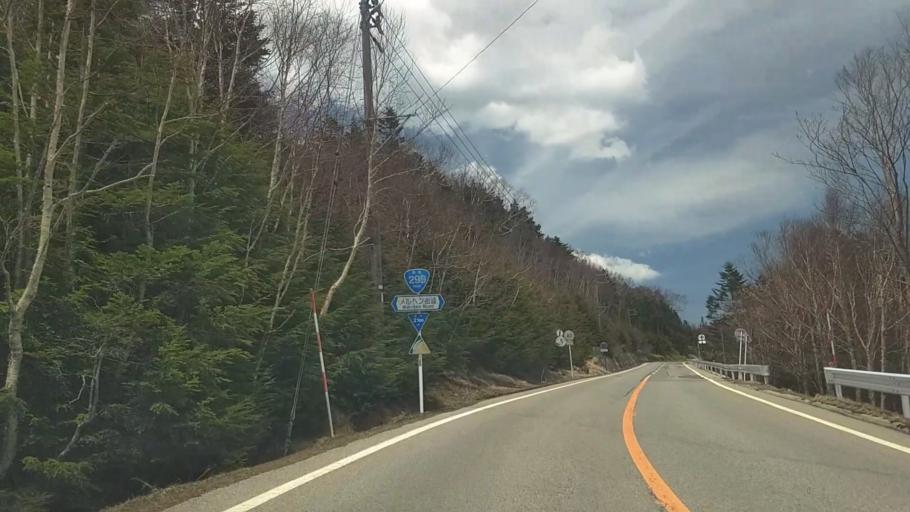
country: JP
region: Nagano
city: Saku
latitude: 36.0553
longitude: 138.3544
